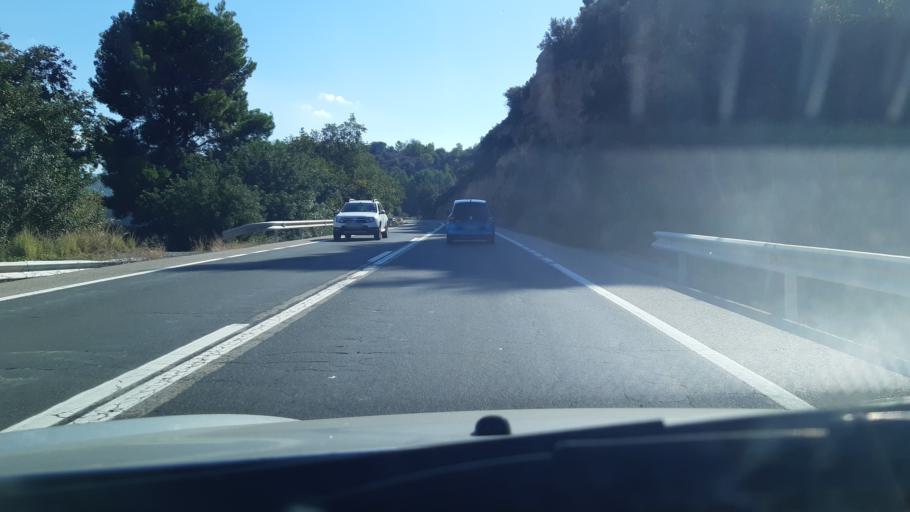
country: ES
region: Catalonia
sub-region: Provincia de Tarragona
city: Tivenys
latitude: 40.8710
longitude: 0.5016
